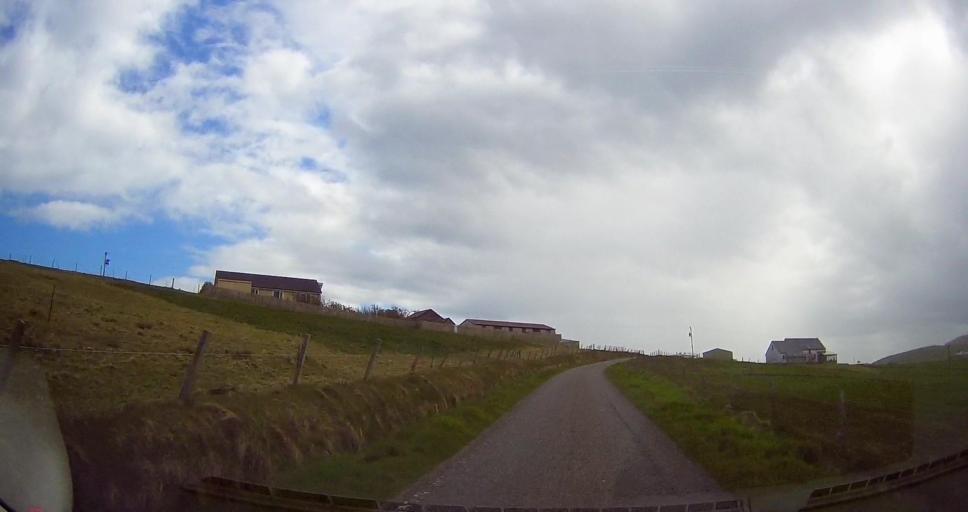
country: GB
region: Scotland
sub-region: Shetland Islands
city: Sandwick
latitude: 59.9175
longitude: -1.3203
